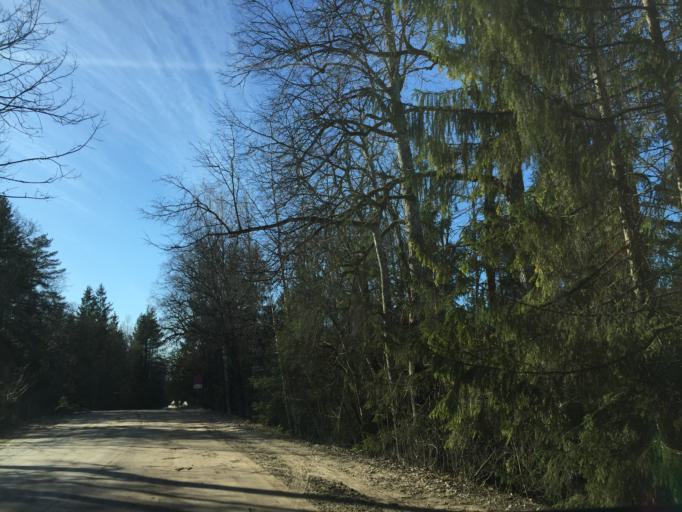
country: LV
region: Ropazu
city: Ropazi
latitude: 56.9196
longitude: 24.7329
